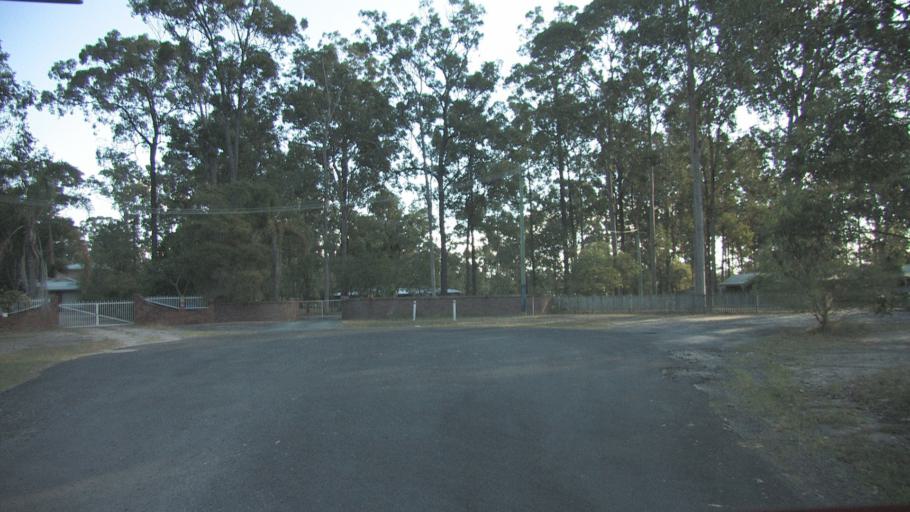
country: AU
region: Queensland
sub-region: Ipswich
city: Springfield Lakes
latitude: -27.7000
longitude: 152.9521
